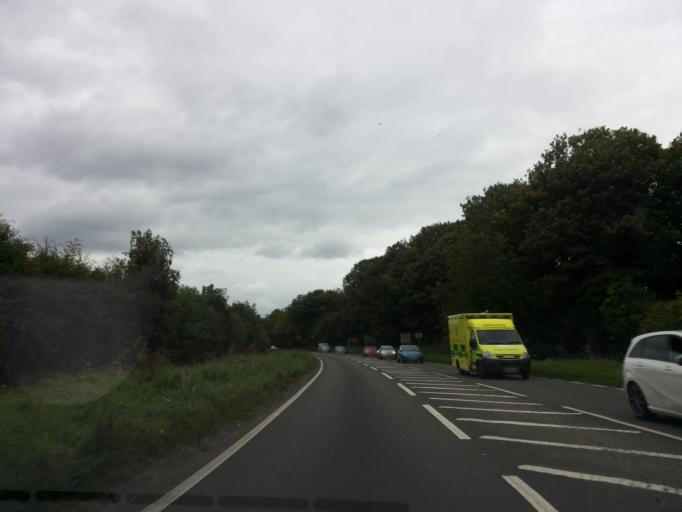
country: GB
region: England
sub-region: Buckinghamshire
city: Great Missenden
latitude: 51.6899
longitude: -0.6917
